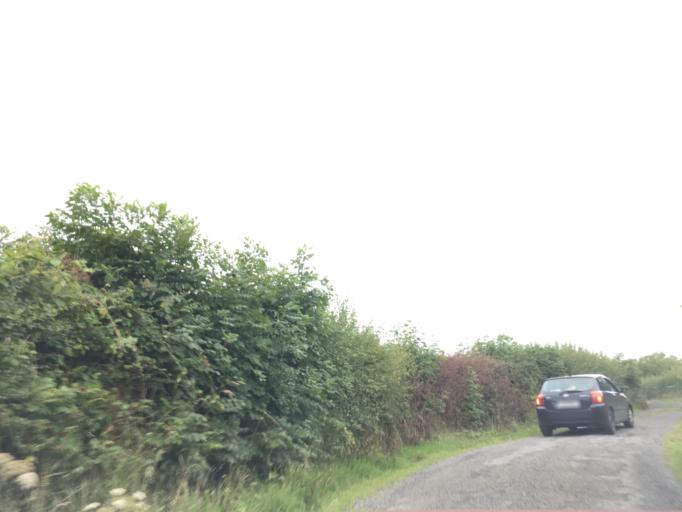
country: IE
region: Munster
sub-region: An Clar
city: Ennis
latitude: 52.7277
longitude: -9.0896
